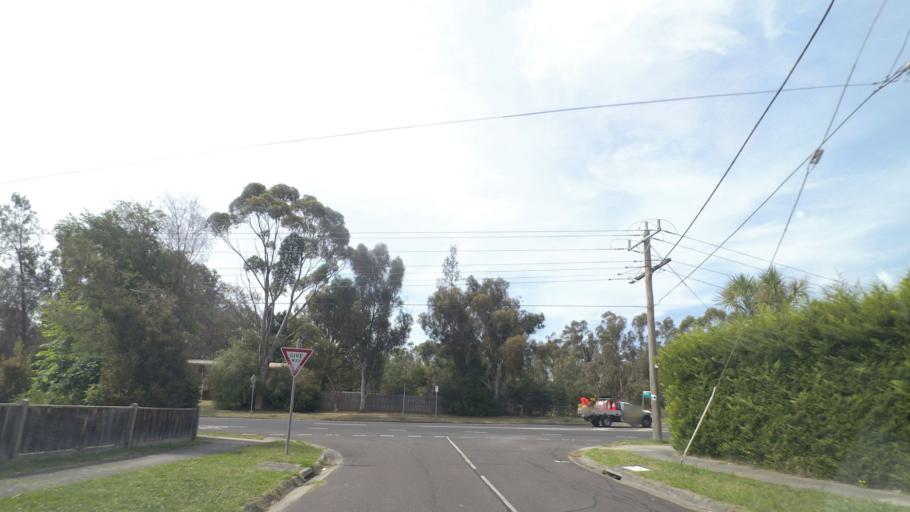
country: AU
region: Victoria
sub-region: Maroondah
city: Croydon North
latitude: -37.7721
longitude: 145.2989
